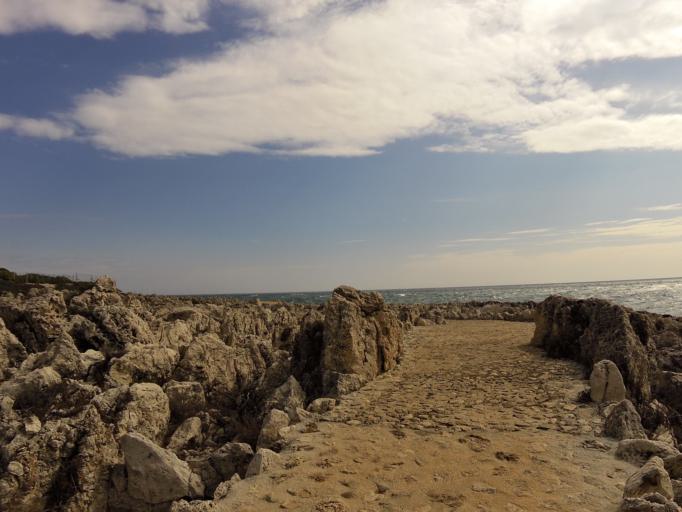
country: FR
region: Provence-Alpes-Cote d'Azur
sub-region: Departement des Alpes-Maritimes
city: Saint-Jean-Cap-Ferrat
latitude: 43.6752
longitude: 7.3305
